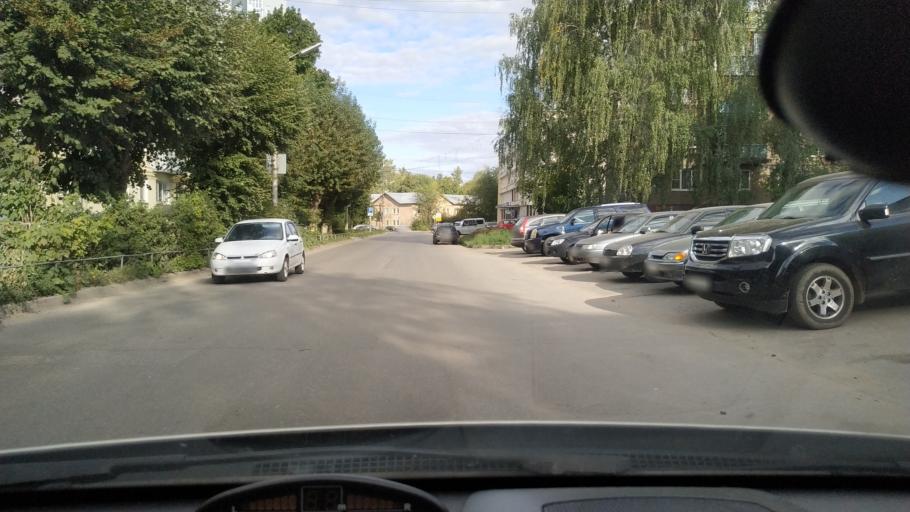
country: RU
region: Rjazan
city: Ryazan'
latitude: 54.6056
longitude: 39.7171
